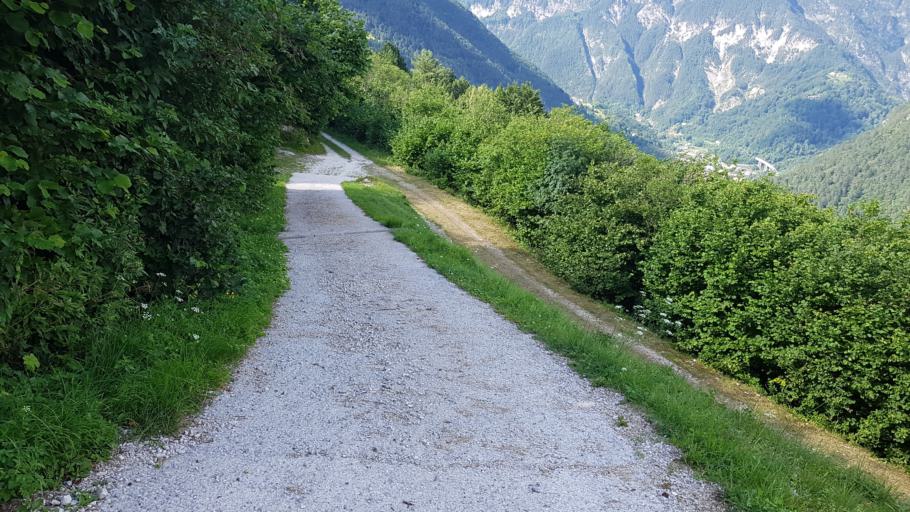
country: IT
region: Friuli Venezia Giulia
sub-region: Provincia di Udine
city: Dogna
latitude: 46.4301
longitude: 13.3071
